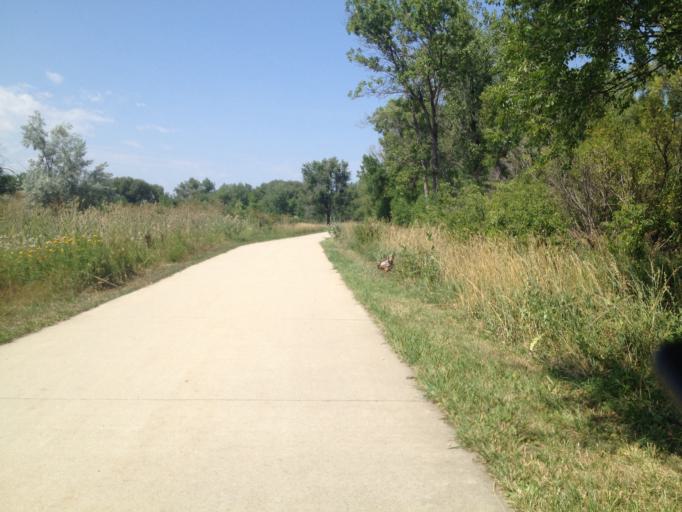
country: US
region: Colorado
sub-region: Boulder County
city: Boulder
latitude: 40.0042
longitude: -105.2163
